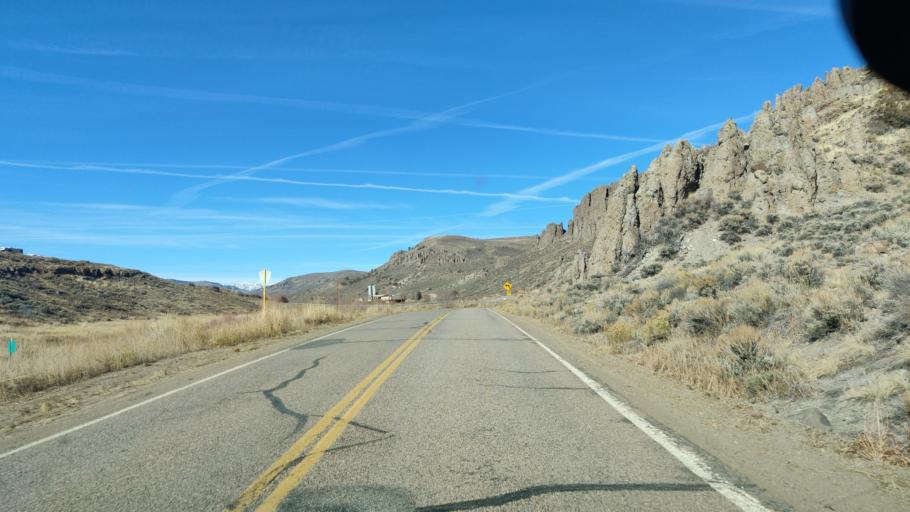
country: US
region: Colorado
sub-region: Gunnison County
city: Gunnison
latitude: 38.5754
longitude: -106.9616
